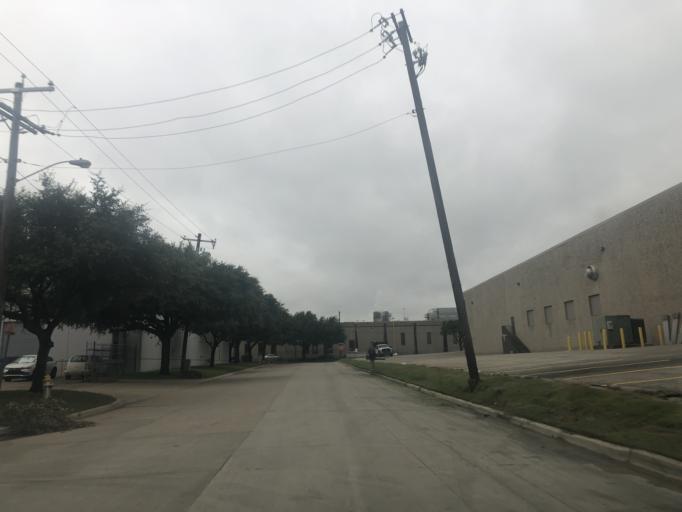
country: US
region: Texas
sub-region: Dallas County
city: Cockrell Hill
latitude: 32.7740
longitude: -96.8585
